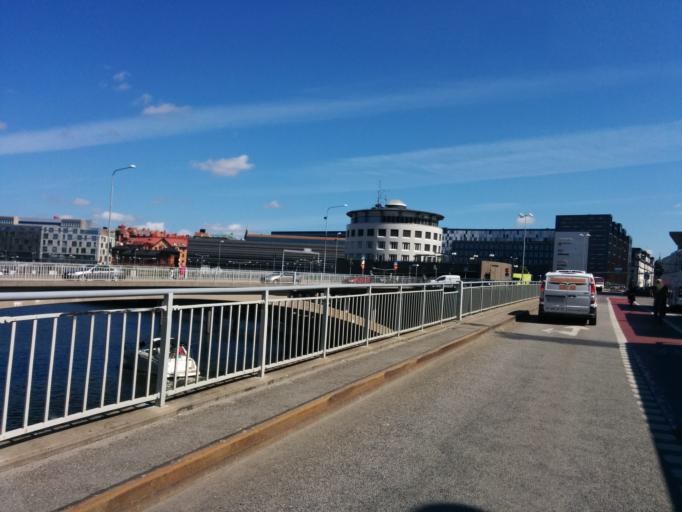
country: SE
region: Stockholm
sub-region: Stockholms Kommun
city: Stockholm
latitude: 59.3318
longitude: 18.0500
